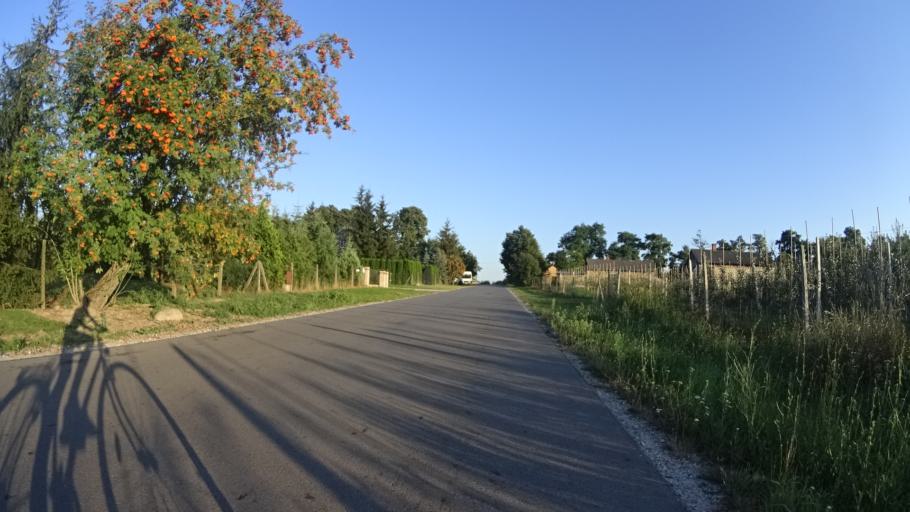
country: PL
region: Masovian Voivodeship
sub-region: Powiat grojecki
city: Goszczyn
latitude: 51.6899
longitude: 20.8181
